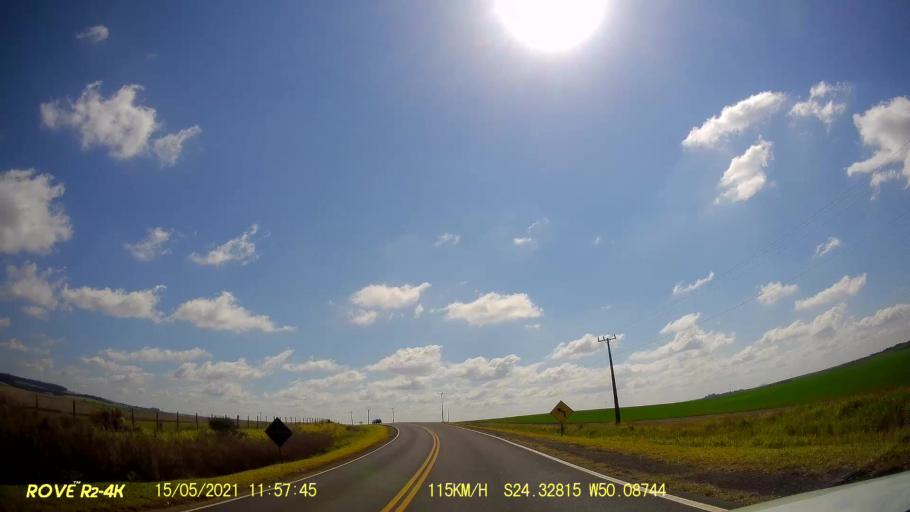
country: BR
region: Parana
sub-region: Pirai Do Sul
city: Pirai do Sul
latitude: -24.3261
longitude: -50.0892
